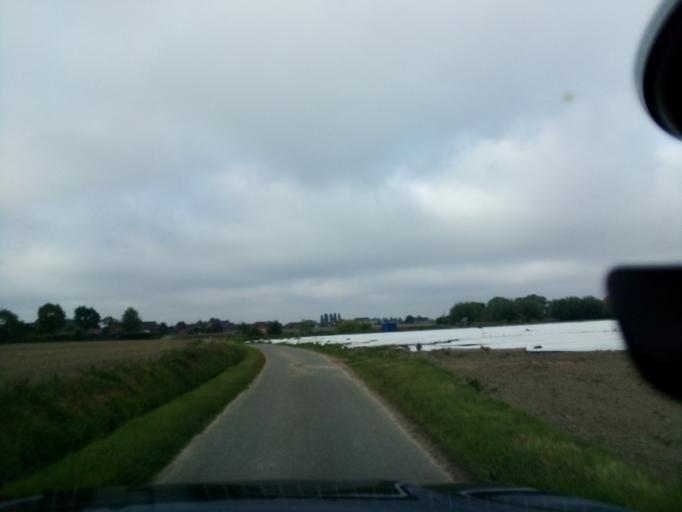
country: BE
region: Flanders
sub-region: Provincie West-Vlaanderen
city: Ingelmunster
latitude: 50.9409
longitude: 3.2638
